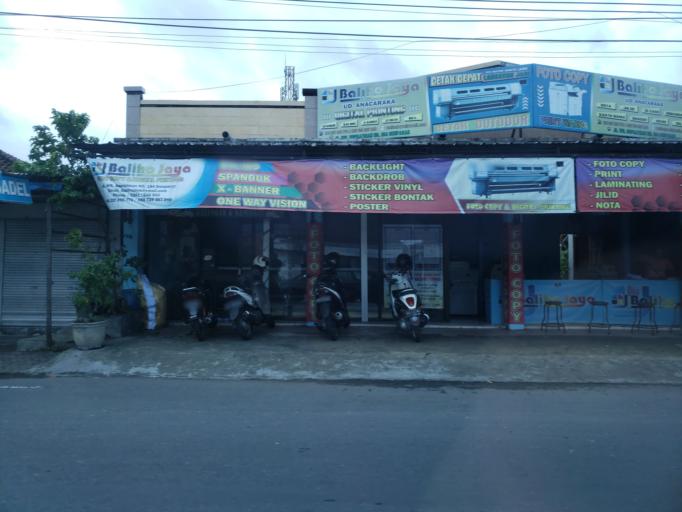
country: ID
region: Bali
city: Dajan Tangluk
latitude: -8.6479
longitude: 115.2418
